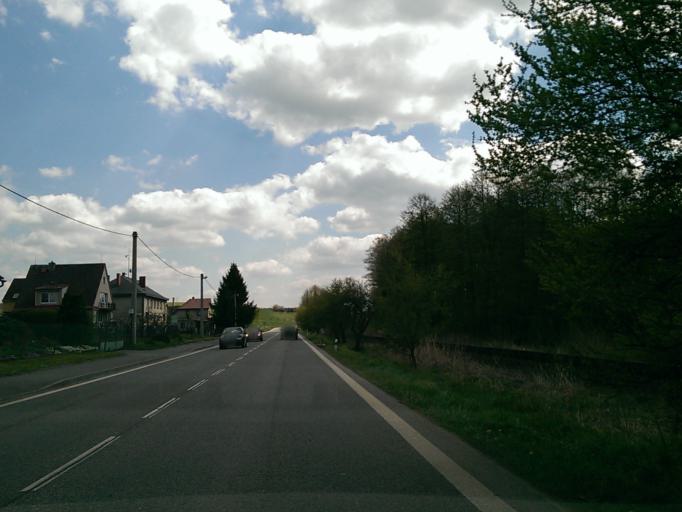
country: CZ
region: Liberecky
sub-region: Okres Semily
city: Turnov
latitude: 50.5597
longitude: 15.2021
